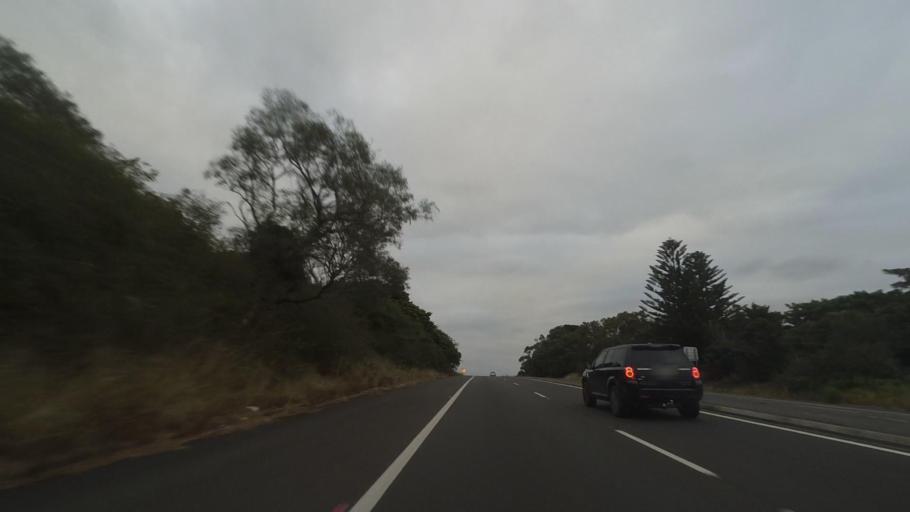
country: AU
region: New South Wales
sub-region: Kiama
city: Kiama
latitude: -34.6751
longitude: 150.8430
